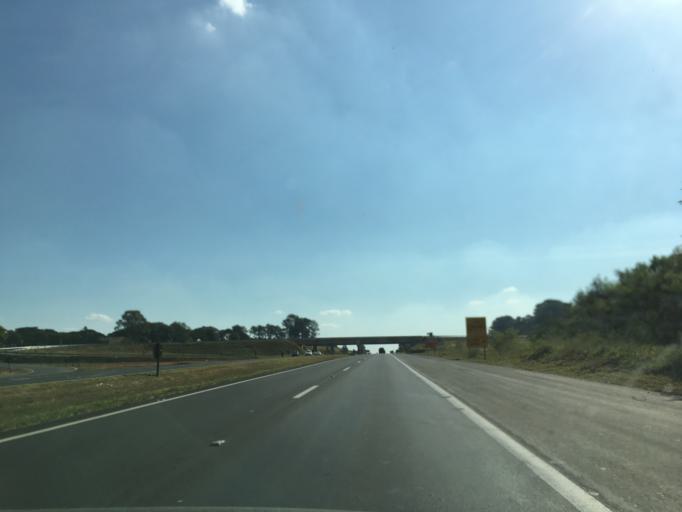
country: BR
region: Sao Paulo
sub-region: Piracicaba
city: Piracicaba
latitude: -22.7219
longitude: -47.6035
